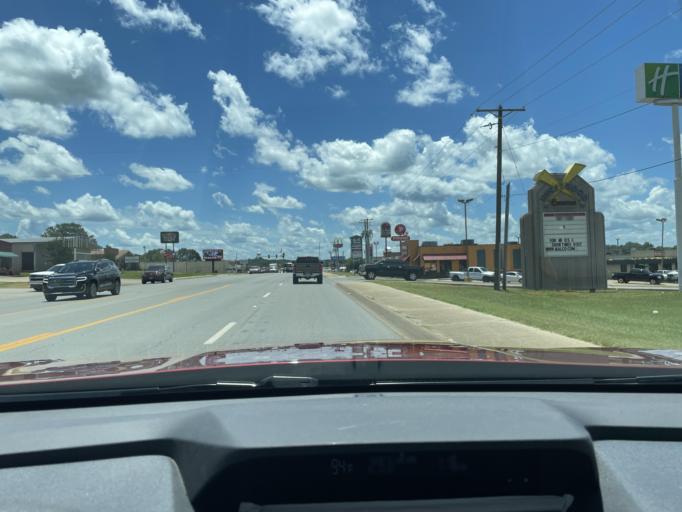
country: US
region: Arkansas
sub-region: Drew County
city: Monticello
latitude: 33.6382
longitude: -91.8015
